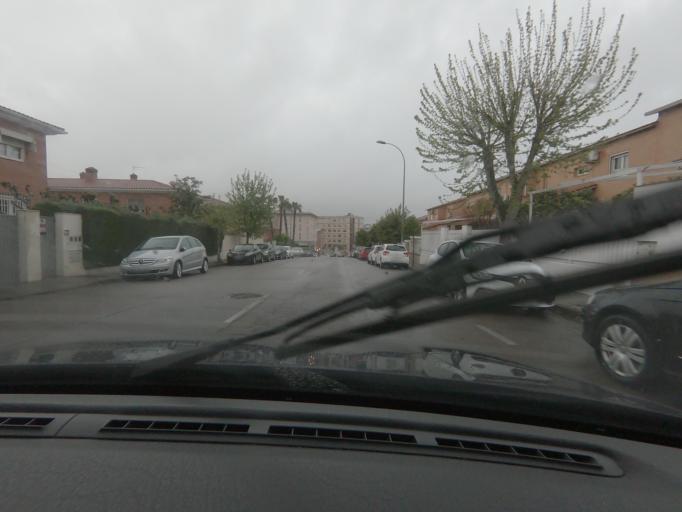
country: ES
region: Extremadura
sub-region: Provincia de Badajoz
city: Merida
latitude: 38.9102
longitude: -6.3628
